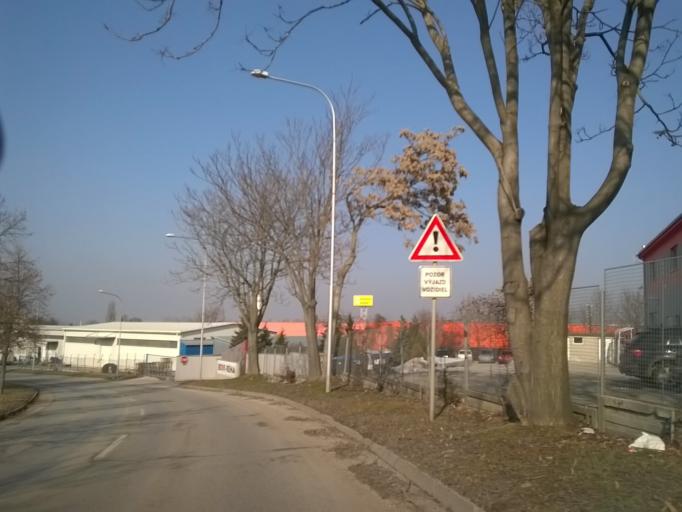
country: SK
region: Nitriansky
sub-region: Okres Nitra
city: Nitra
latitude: 48.3080
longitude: 18.0673
